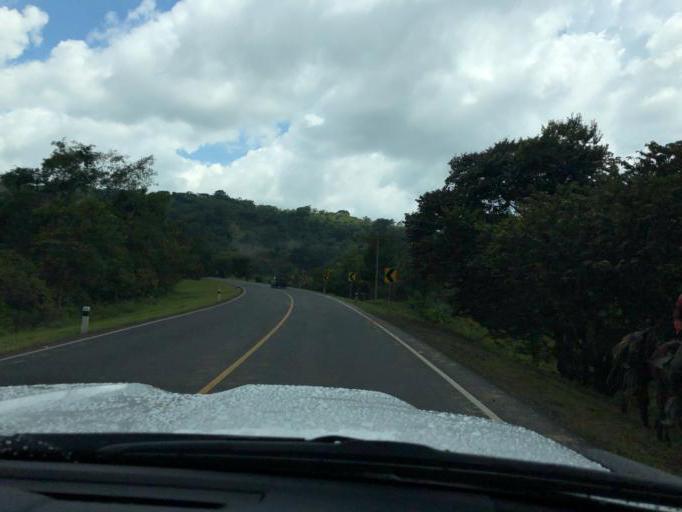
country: NI
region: Chontales
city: Villa Sandino
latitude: 11.9958
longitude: -84.9354
